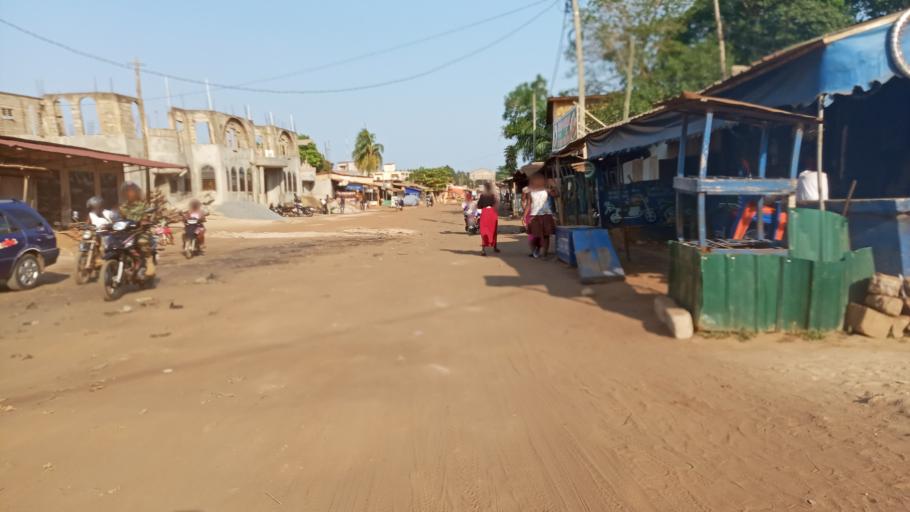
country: TG
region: Maritime
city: Lome
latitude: 6.1813
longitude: 1.1664
